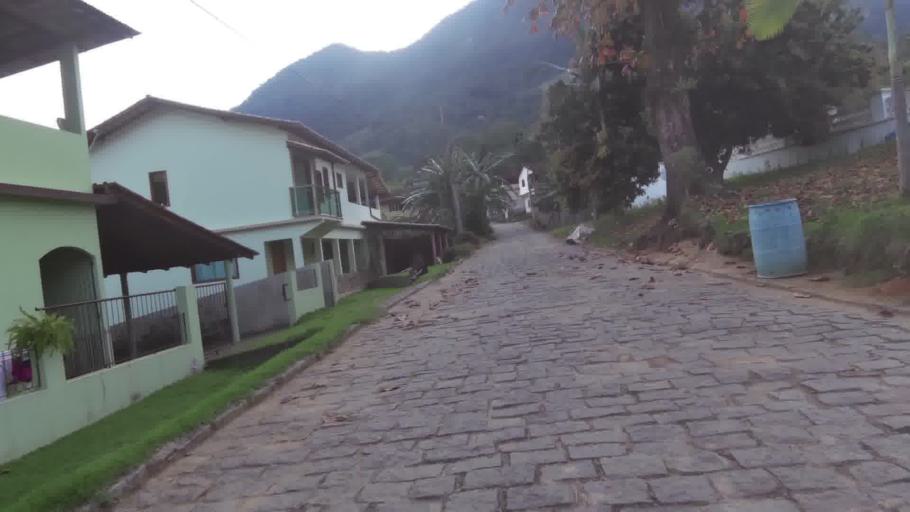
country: BR
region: Espirito Santo
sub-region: Alfredo Chaves
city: Alfredo Chaves
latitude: -20.5799
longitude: -40.6989
